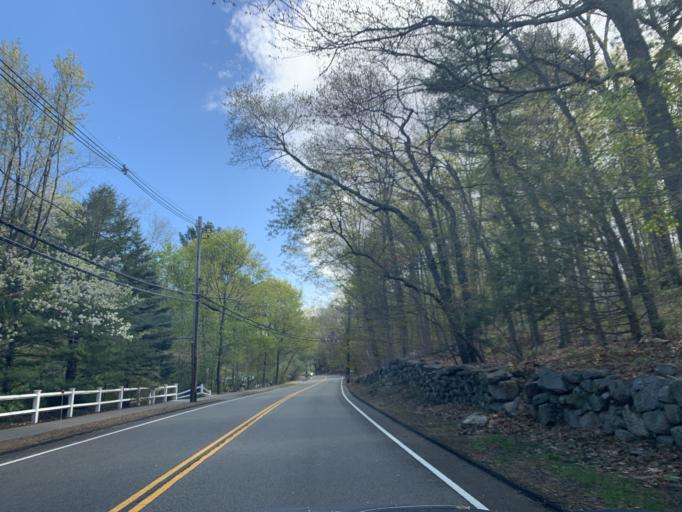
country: US
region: Massachusetts
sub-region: Norfolk County
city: Milton
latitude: 42.2347
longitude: -71.1086
